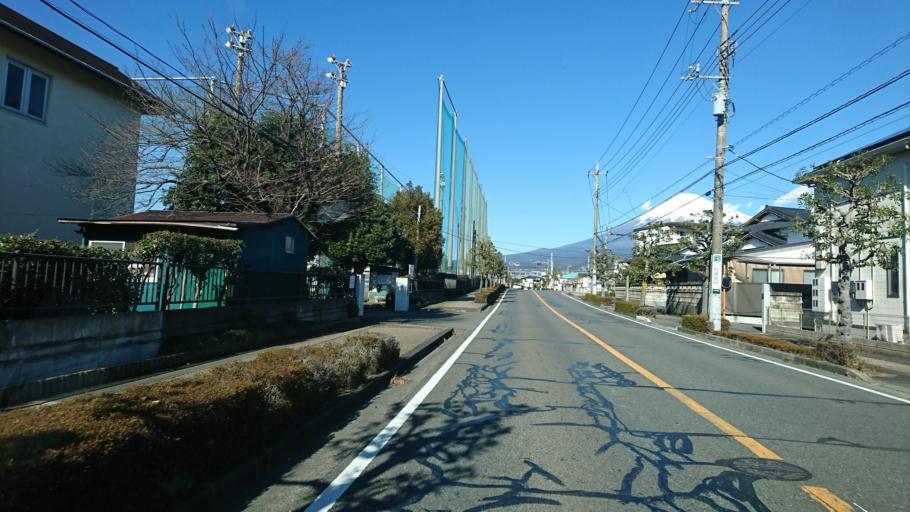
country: JP
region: Shizuoka
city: Fuji
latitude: 35.1672
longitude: 138.6535
